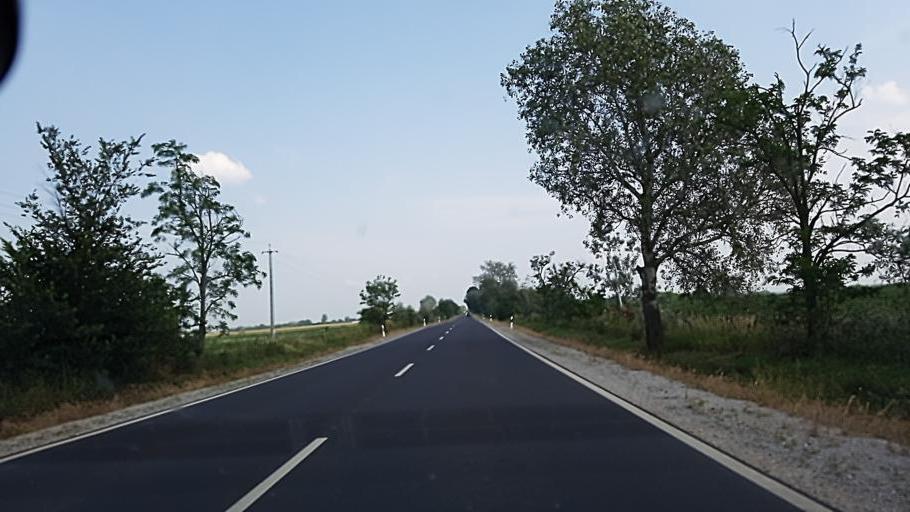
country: HU
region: Heves
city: Besenyotelek
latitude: 47.6839
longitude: 20.4856
